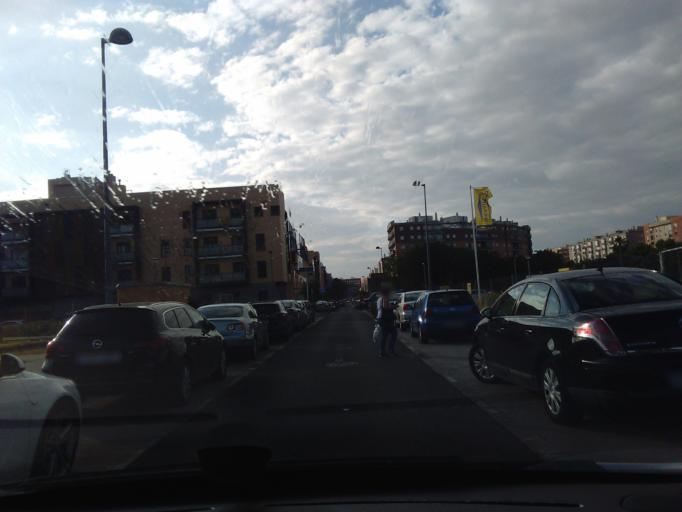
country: ES
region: Andalusia
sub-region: Provincia de Sevilla
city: Sevilla
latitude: 37.3948
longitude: -5.9232
